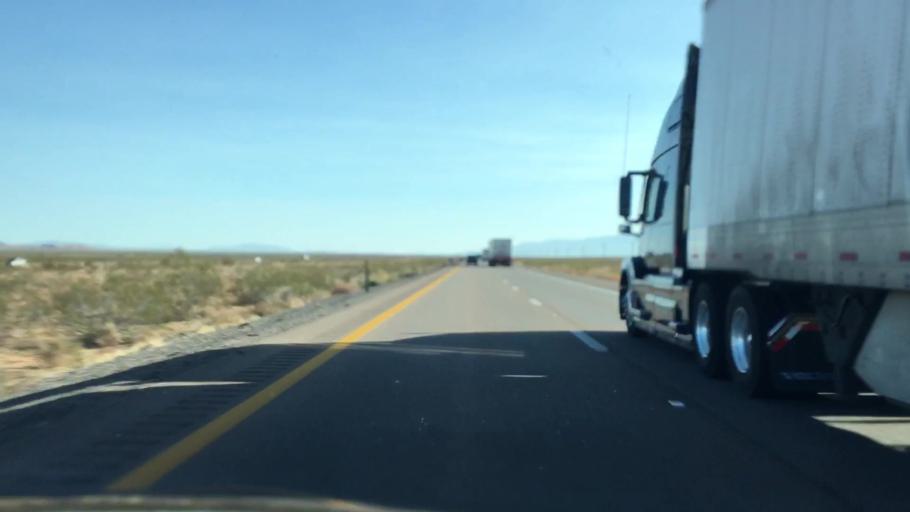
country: US
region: Nevada
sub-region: Clark County
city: Moapa Valley
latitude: 36.7489
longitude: -114.4050
